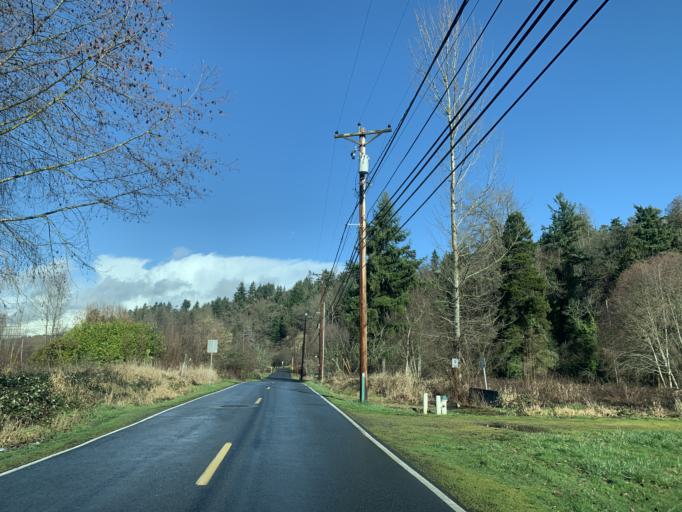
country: US
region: Washington
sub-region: Pierce County
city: Fife Heights
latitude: 47.2475
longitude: -122.3468
